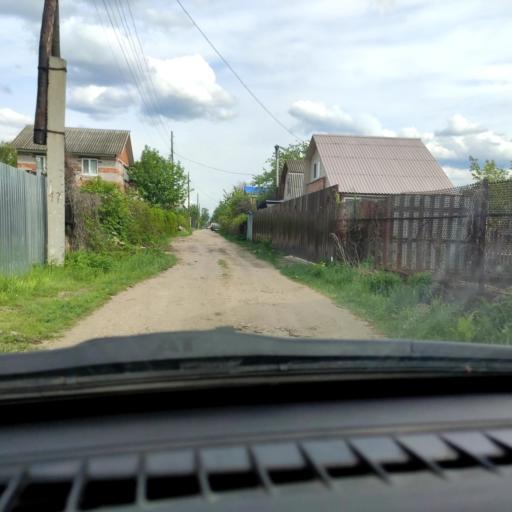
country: RU
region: Samara
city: Zhigulevsk
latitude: 53.4590
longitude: 49.5205
